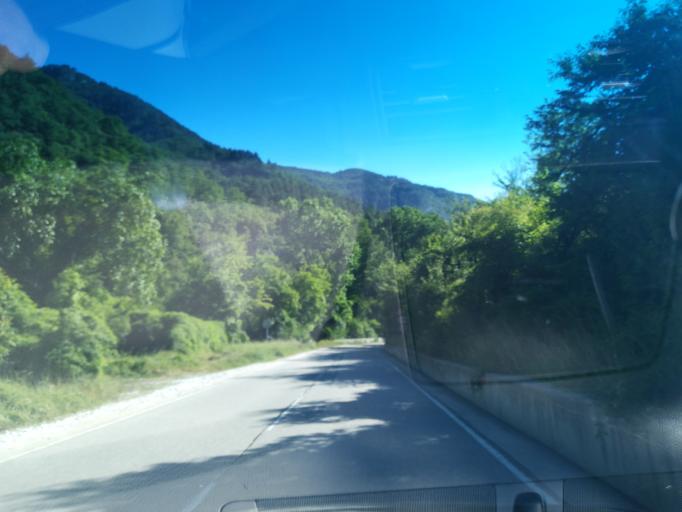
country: BG
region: Plovdiv
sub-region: Obshtina Luki
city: Luki
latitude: 41.8960
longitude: 24.7280
